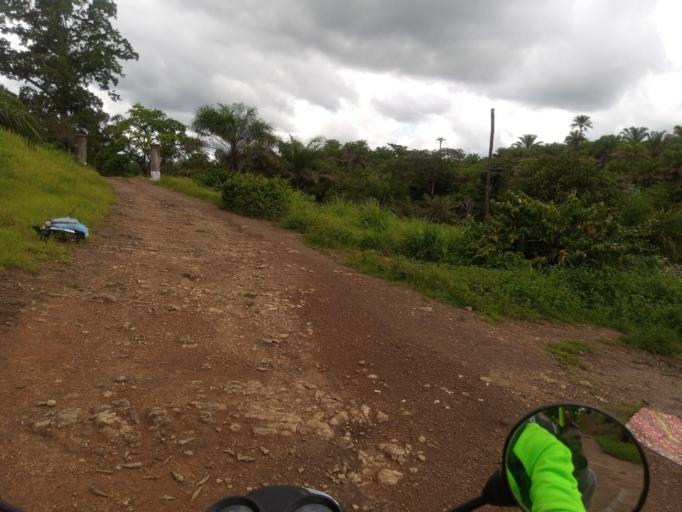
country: SL
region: Northern Province
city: Port Loko
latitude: 8.7609
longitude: -12.7754
